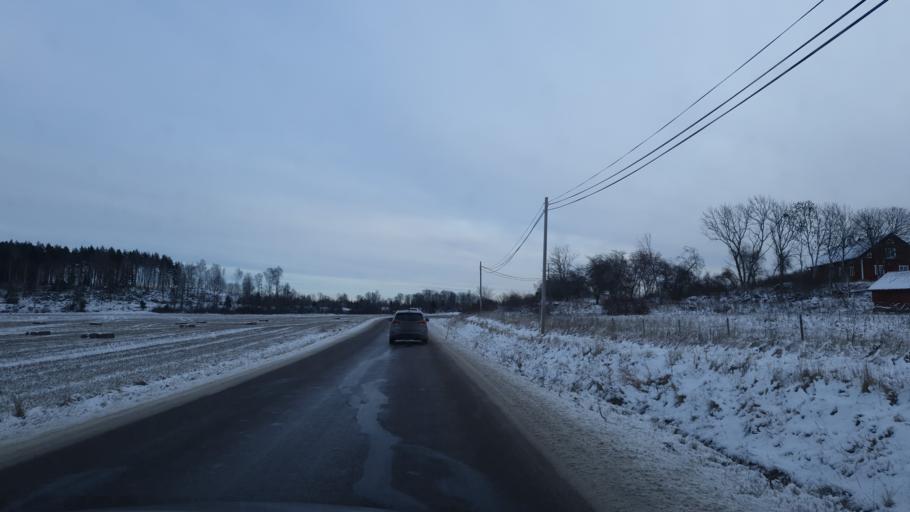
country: SE
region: Uppsala
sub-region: Habo Kommun
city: Balsta
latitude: 59.7087
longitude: 17.5653
